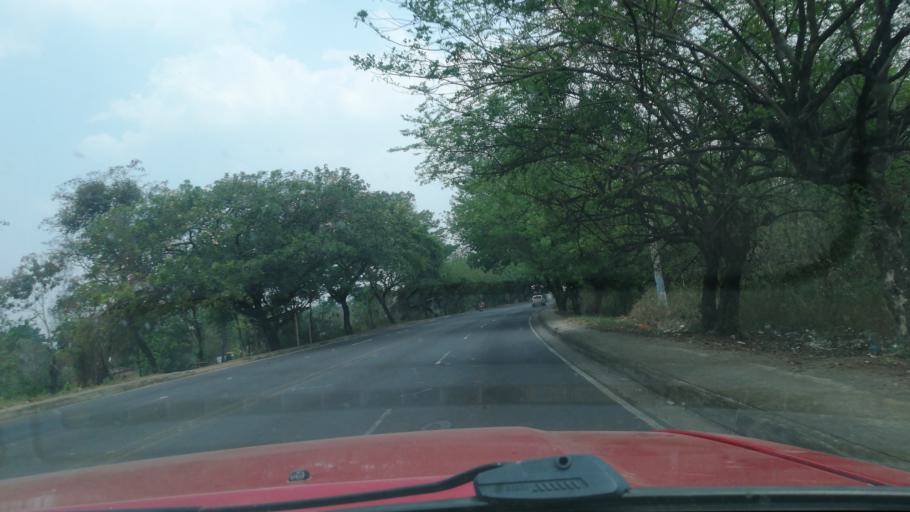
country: SV
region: Santa Ana
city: Santa Ana
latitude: 13.9798
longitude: -89.5955
